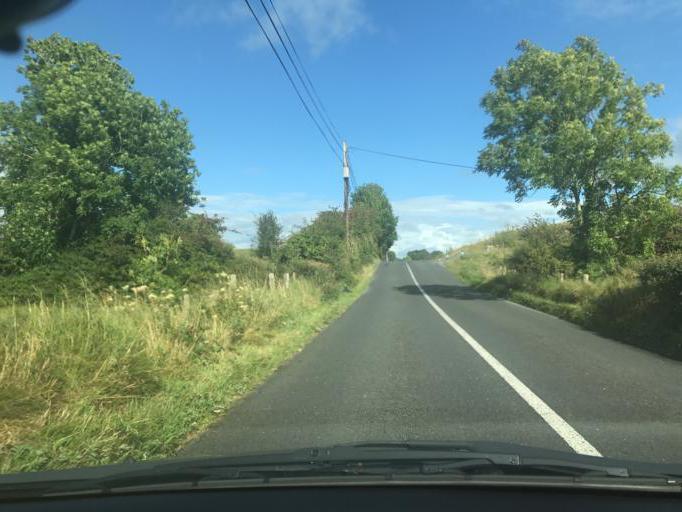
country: IE
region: Connaught
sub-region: Sligo
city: Collooney
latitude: 54.1888
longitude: -8.4539
